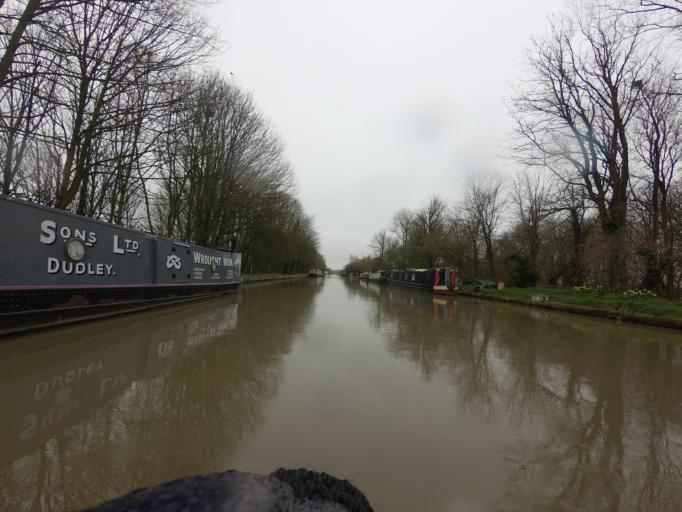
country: GB
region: England
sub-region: Milton Keynes
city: Stony Stratford
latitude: 52.0714
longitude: -0.8386
